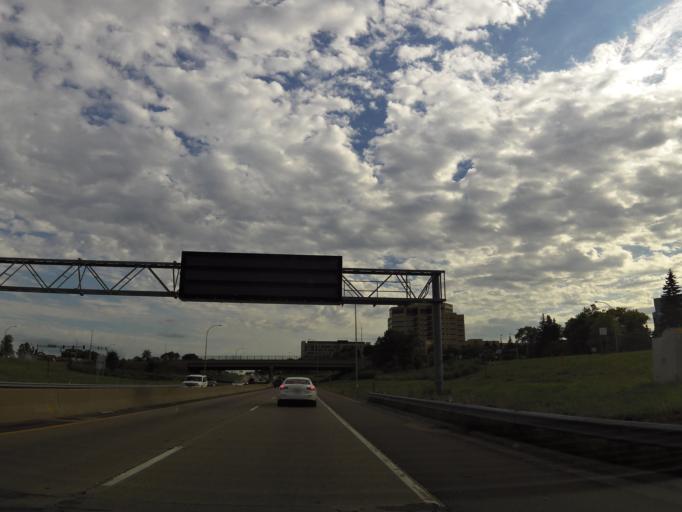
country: US
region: Minnesota
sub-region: Hennepin County
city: Edina
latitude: 44.9007
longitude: -93.4016
